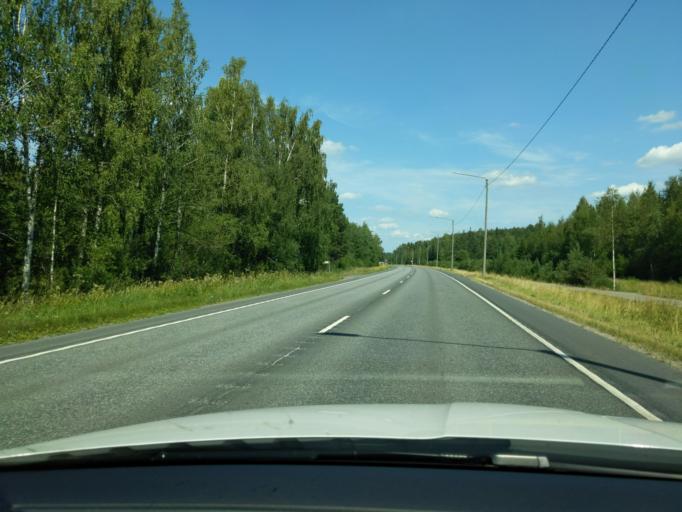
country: FI
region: Uusimaa
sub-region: Helsinki
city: Kerava
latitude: 60.3687
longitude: 25.1294
